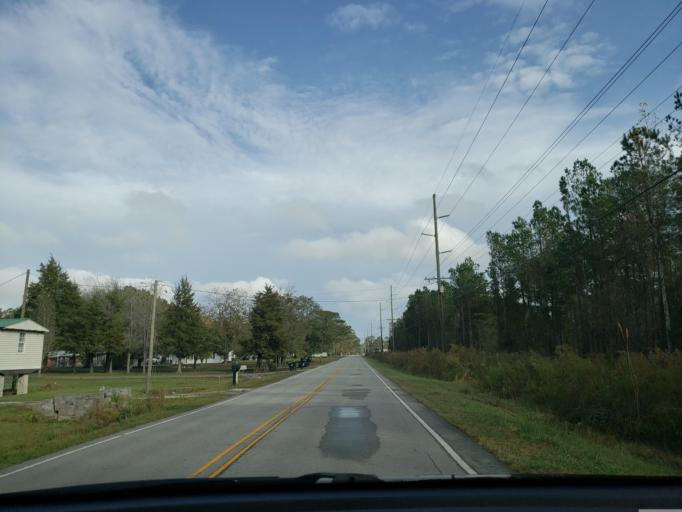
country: US
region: North Carolina
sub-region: Onslow County
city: Jacksonville
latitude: 34.6860
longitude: -77.5163
